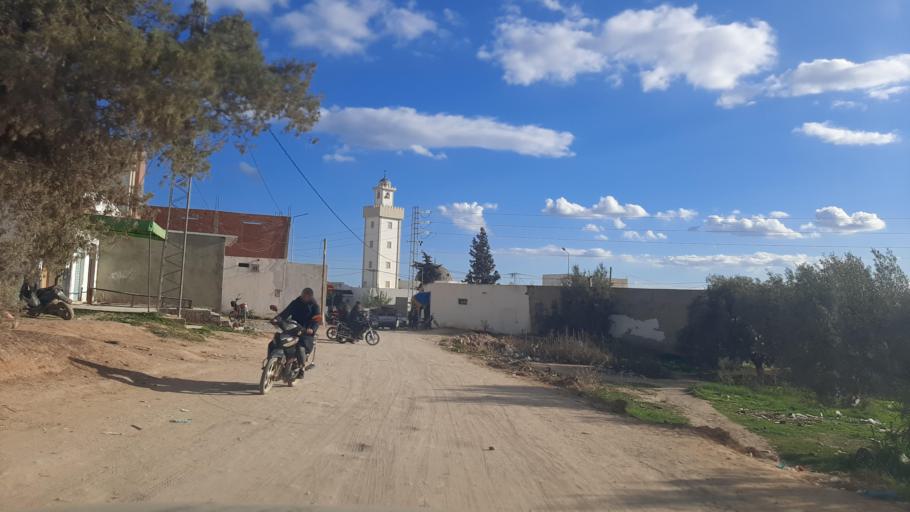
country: TN
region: Nabul
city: Al Hammamat
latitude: 36.4174
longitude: 10.5149
